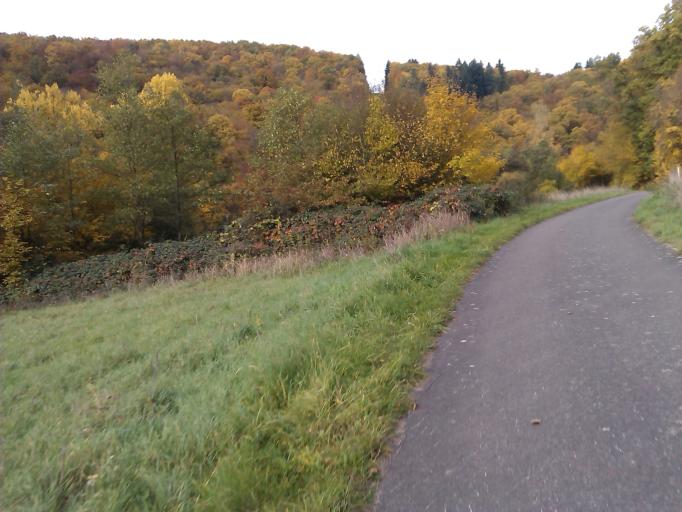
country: DE
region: Rheinland-Pfalz
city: Oberweiler-Tiefenbach
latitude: 49.6136
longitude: 7.6146
